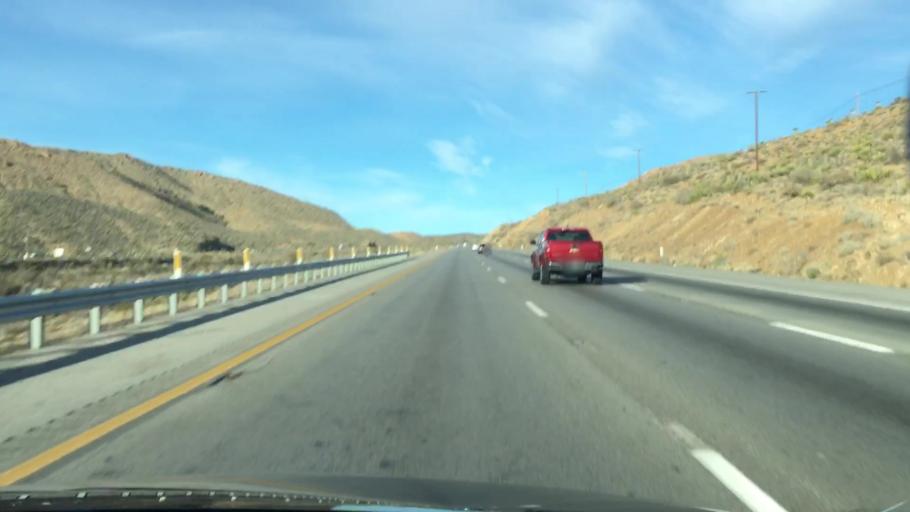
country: US
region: Nevada
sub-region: Clark County
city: Sandy Valley
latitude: 35.4684
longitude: -115.4900
